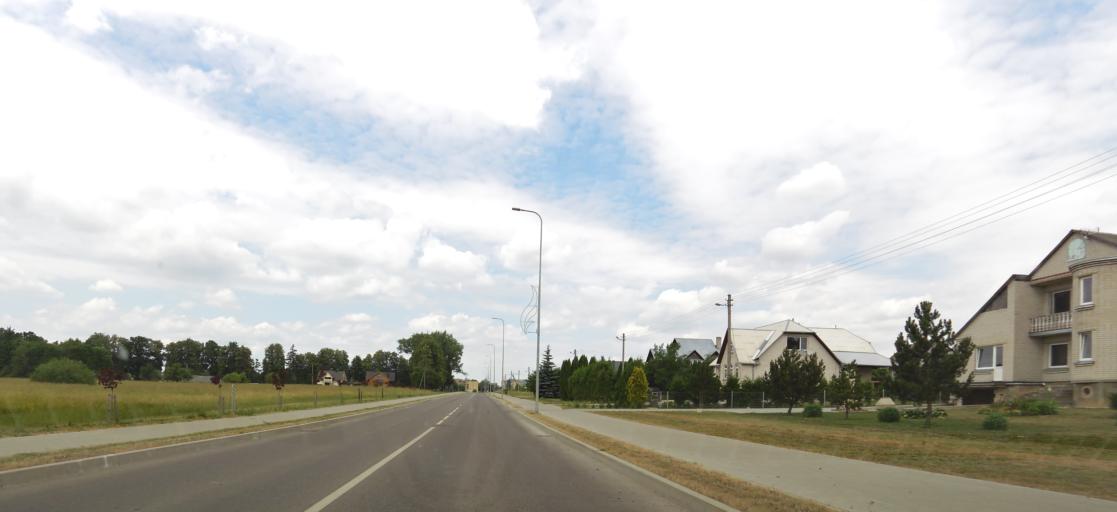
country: LT
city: Sirvintos
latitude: 55.0431
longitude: 24.9659
